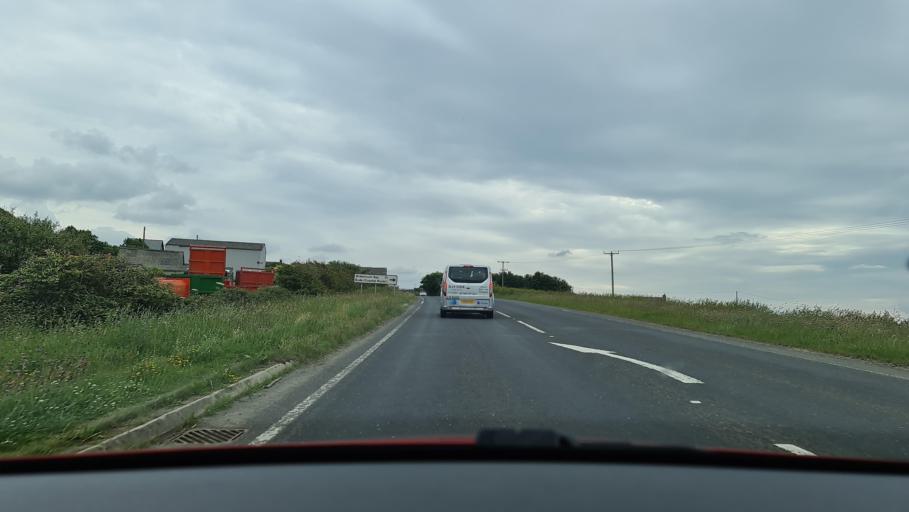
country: GB
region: England
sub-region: Cornwall
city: Poundstock
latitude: 50.7784
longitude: -4.5408
